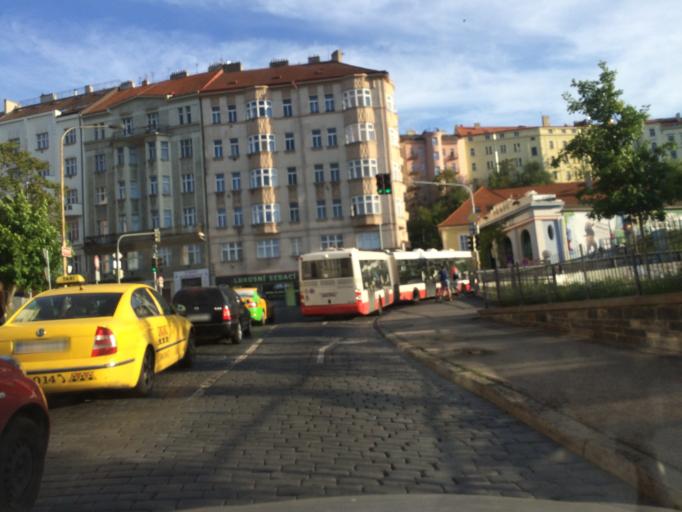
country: CZ
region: Praha
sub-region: Praha 8
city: Karlin
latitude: 50.0878
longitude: 14.4432
